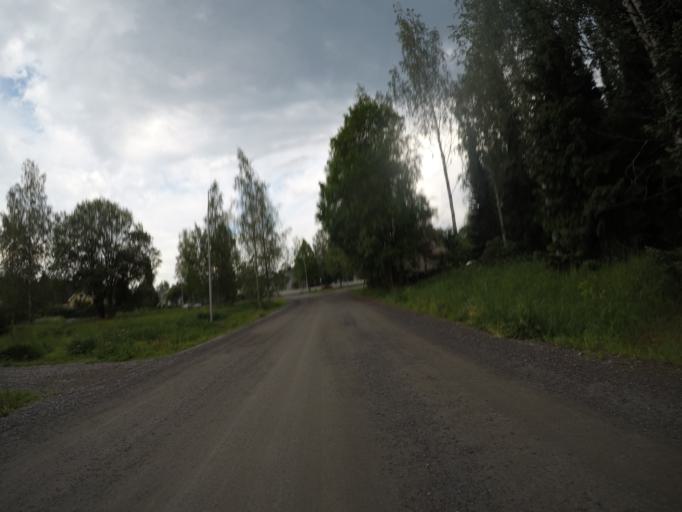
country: FI
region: Haeme
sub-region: Haemeenlinna
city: Haemeenlinna
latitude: 61.0088
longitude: 24.4967
